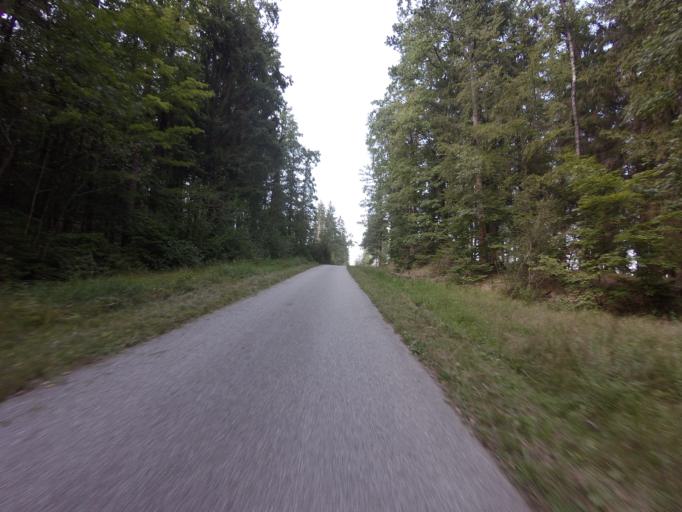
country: CZ
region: Jihocesky
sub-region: Okres Ceske Budejovice
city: Hluboka nad Vltavou
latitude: 49.1037
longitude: 14.4615
